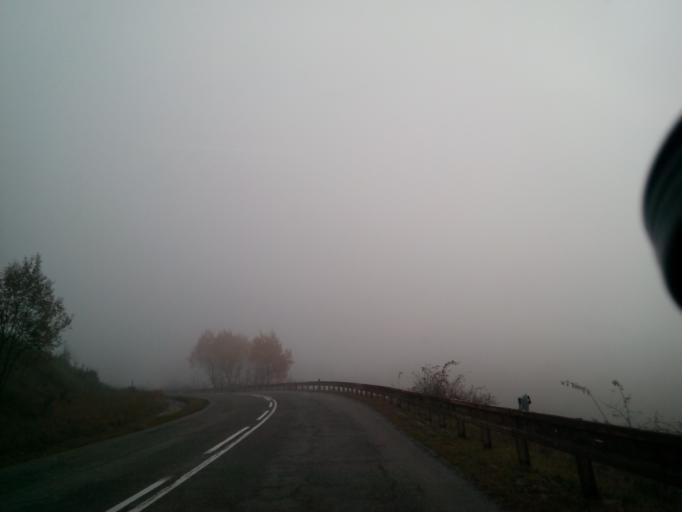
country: SK
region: Kosicky
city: Gelnica
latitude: 48.8514
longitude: 21.0294
